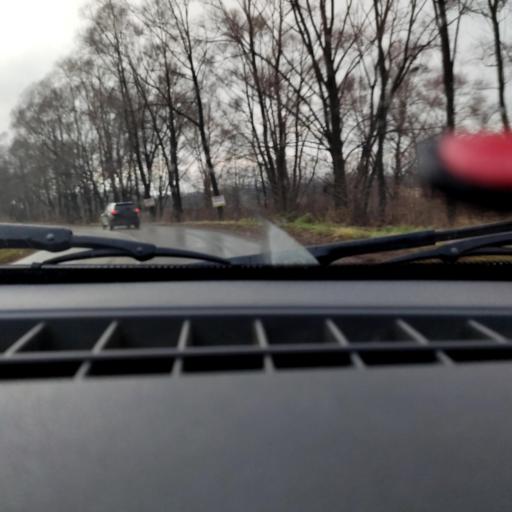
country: RU
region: Bashkortostan
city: Avdon
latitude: 54.5107
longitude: 55.8677
